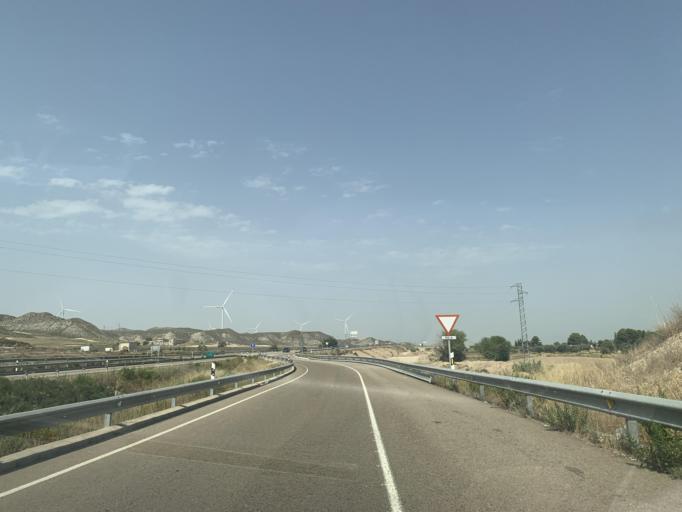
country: ES
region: Aragon
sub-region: Provincia de Zaragoza
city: El Burgo de Ebro
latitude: 41.5459
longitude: -0.6982
